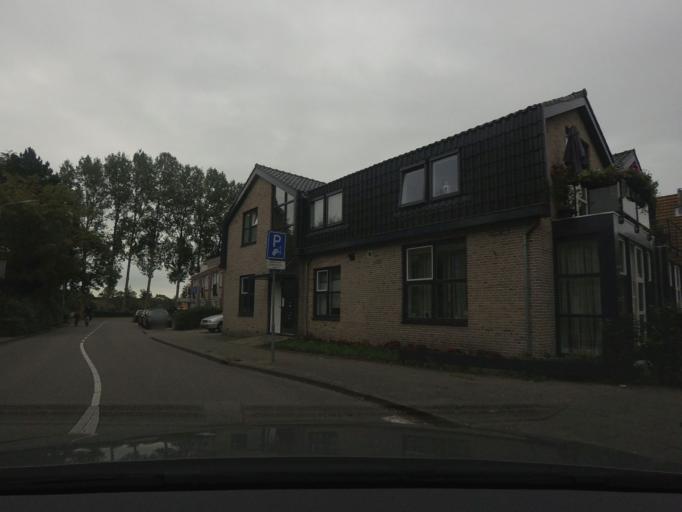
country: NL
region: North Holland
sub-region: Gemeente Schagen
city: Harenkarspel
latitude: 52.7038
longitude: 4.6930
